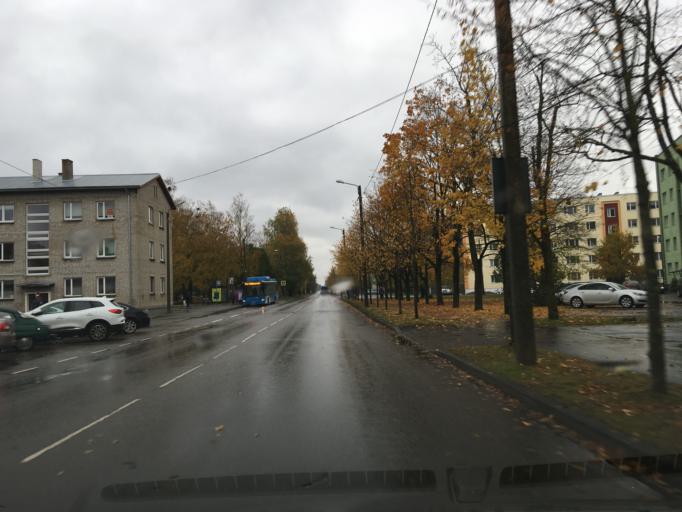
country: EE
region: Paernumaa
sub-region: Paernu linn
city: Parnu
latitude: 58.3732
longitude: 24.5326
